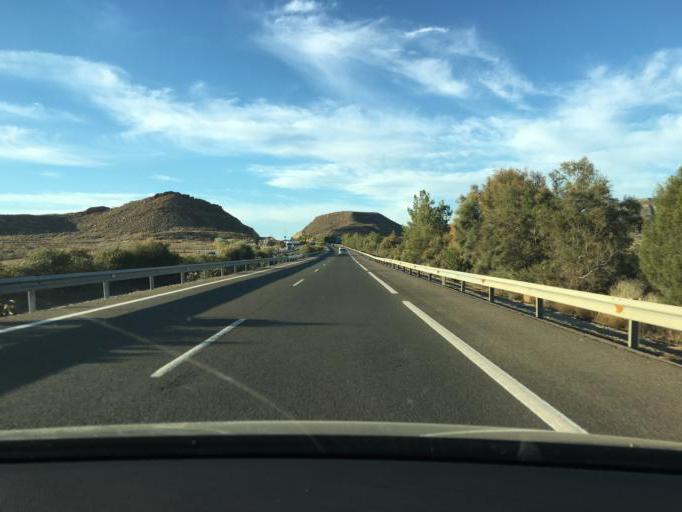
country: ES
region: Andalusia
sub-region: Provincia de Almeria
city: Sorbas
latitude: 37.0544
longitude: -2.0507
